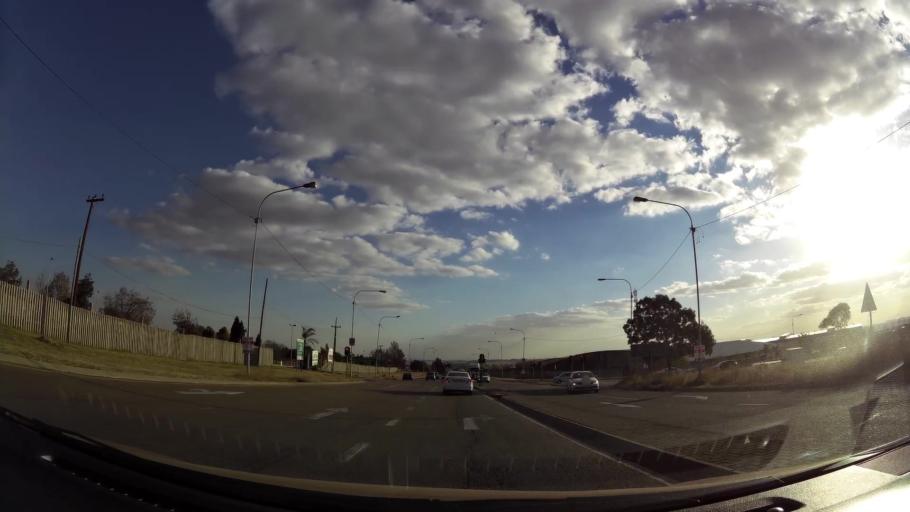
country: ZA
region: Gauteng
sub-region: City of Johannesburg Metropolitan Municipality
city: Midrand
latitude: -25.9282
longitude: 28.1553
